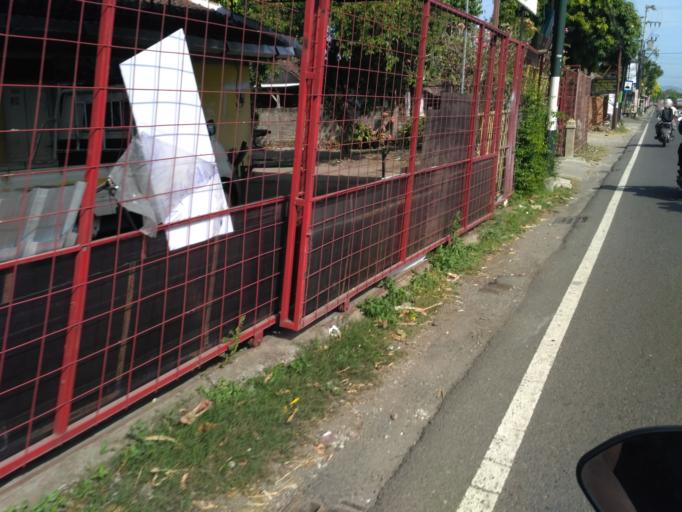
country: ID
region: Daerah Istimewa Yogyakarta
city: Depok
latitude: -7.7771
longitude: 110.4305
